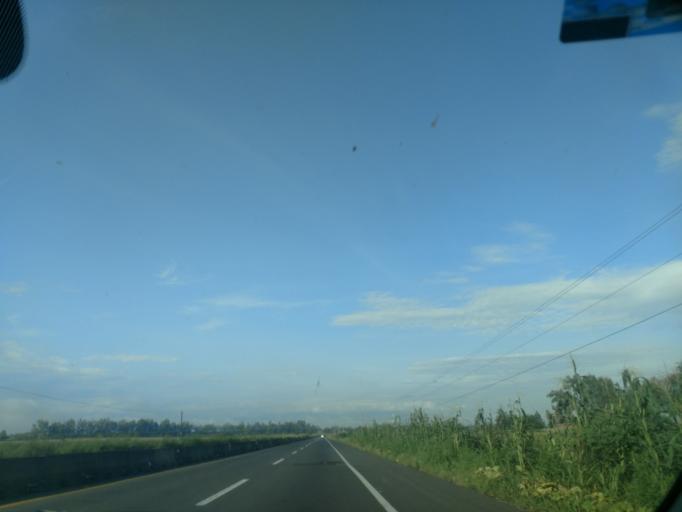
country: MX
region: Jalisco
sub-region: Ameca
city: Los Pocitos
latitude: 20.5415
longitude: -103.9191
